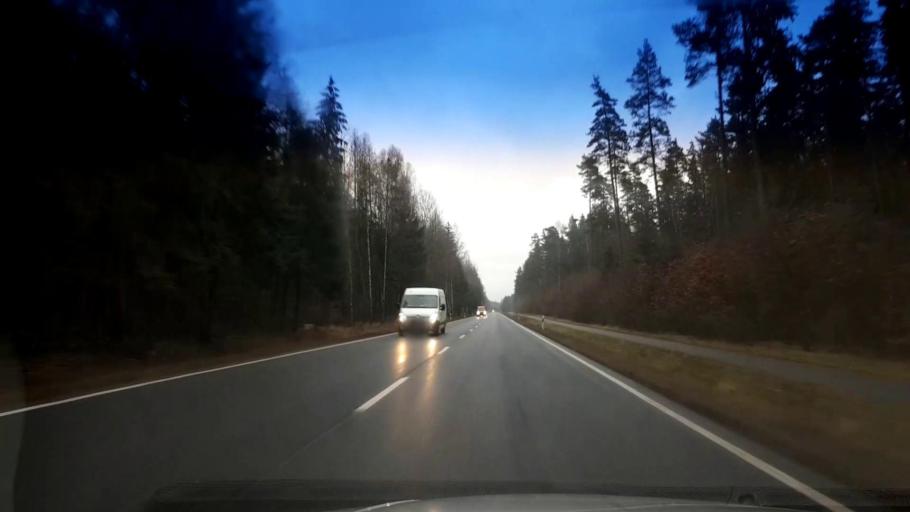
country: DE
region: Bavaria
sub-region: Upper Palatinate
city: Leonberg
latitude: 49.9211
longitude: 12.2893
